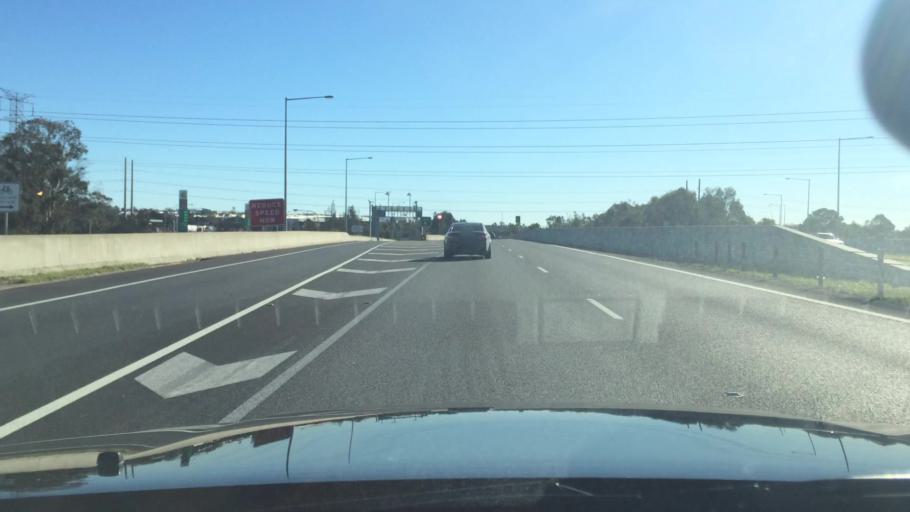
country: AU
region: New South Wales
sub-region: Fairfield
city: Horsley Park
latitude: -33.8157
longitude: 150.8518
